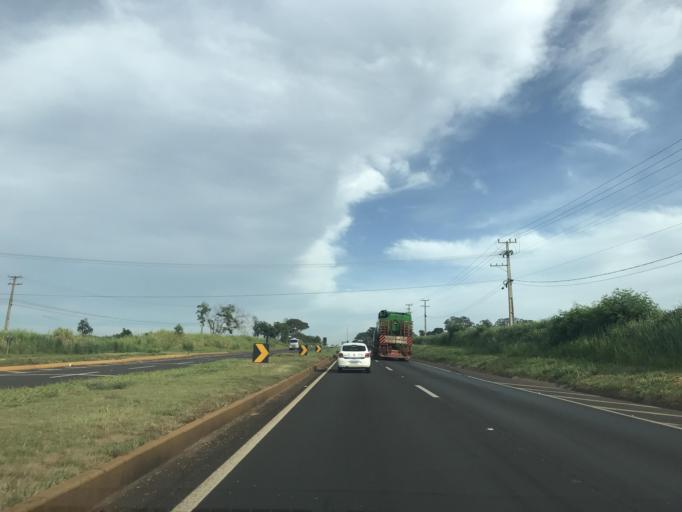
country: BR
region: Parana
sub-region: Maringa
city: Maringa
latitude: -23.4035
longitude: -51.9959
